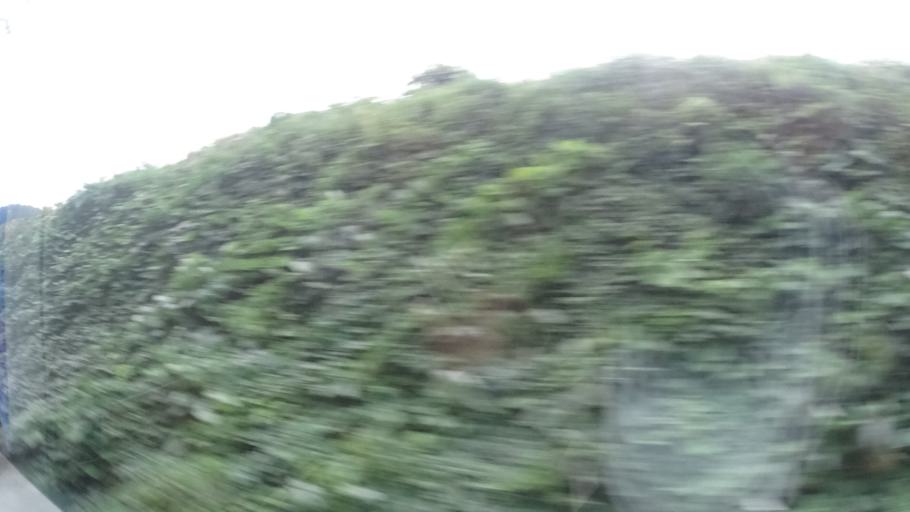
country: JP
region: Yamagata
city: Tsuruoka
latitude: 38.6017
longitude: 139.5713
